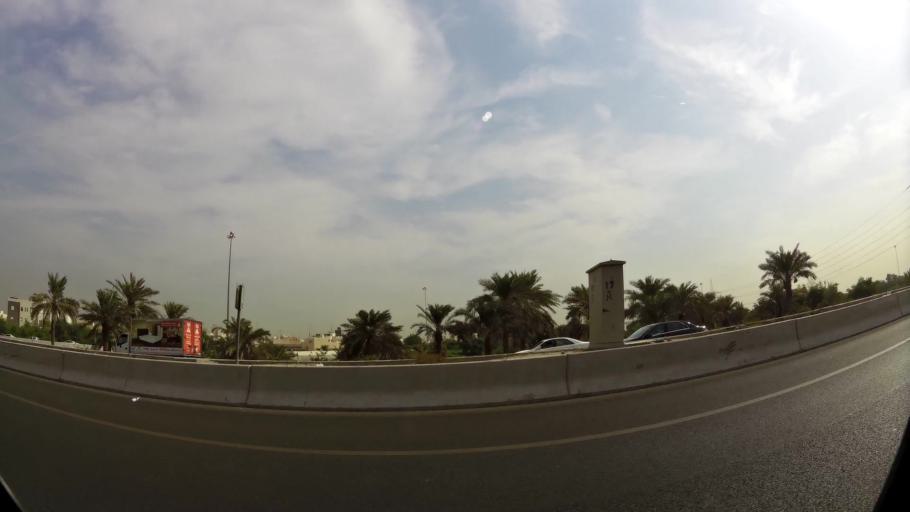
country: KW
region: Al Farwaniyah
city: Al Farwaniyah
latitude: 29.3048
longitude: 47.9787
